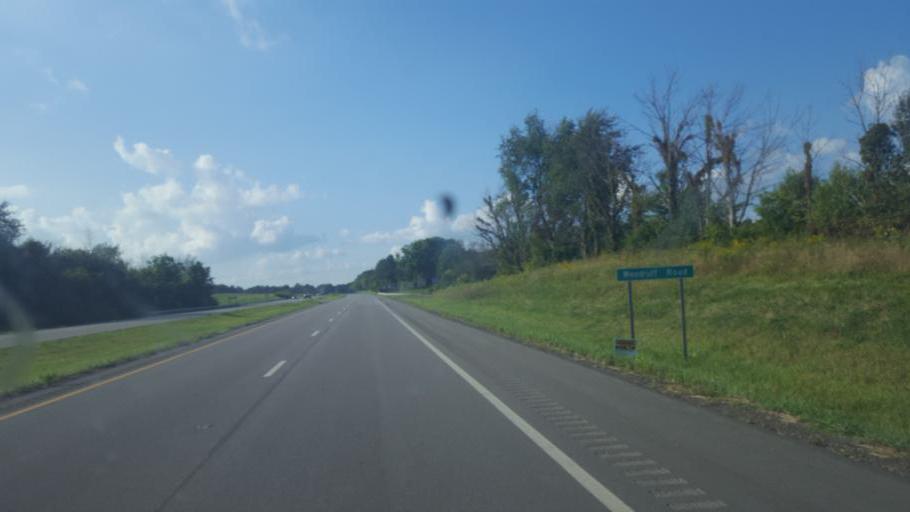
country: US
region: Ohio
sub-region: Sandusky County
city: Bellville
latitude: 40.6618
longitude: -82.5148
